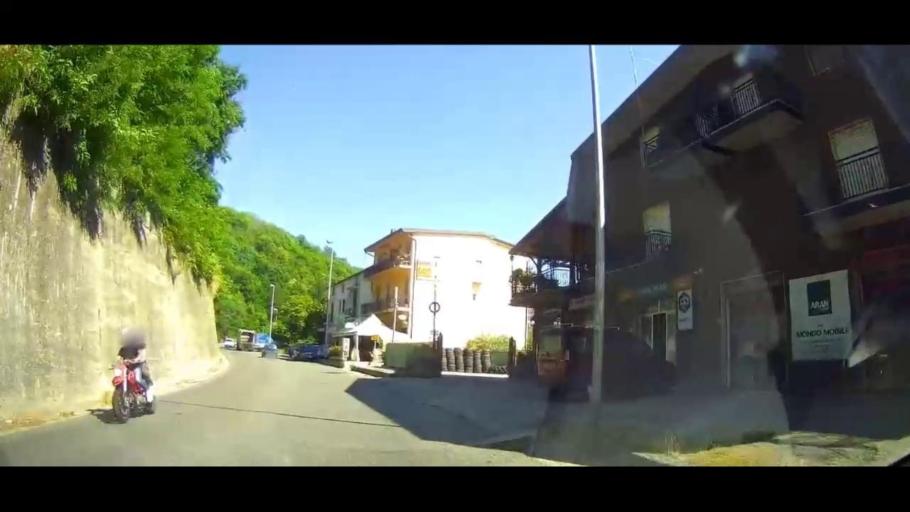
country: IT
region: Calabria
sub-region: Provincia di Cosenza
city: Spezzano della Sila
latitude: 39.3003
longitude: 16.3412
